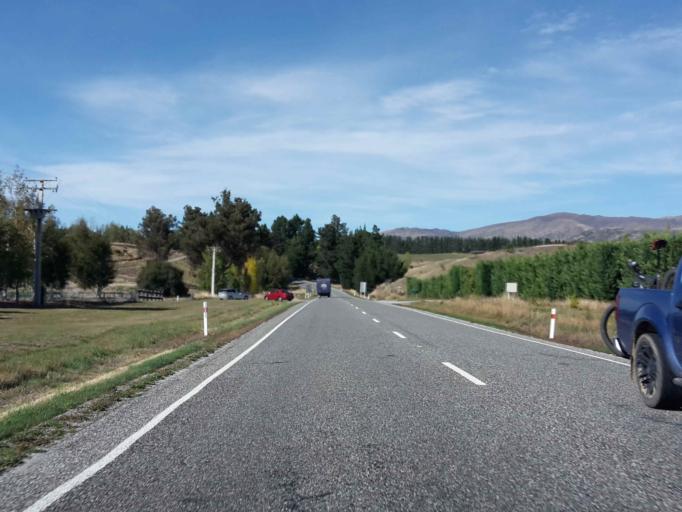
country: NZ
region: Otago
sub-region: Queenstown-Lakes District
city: Wanaka
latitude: -44.7025
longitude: 169.1946
